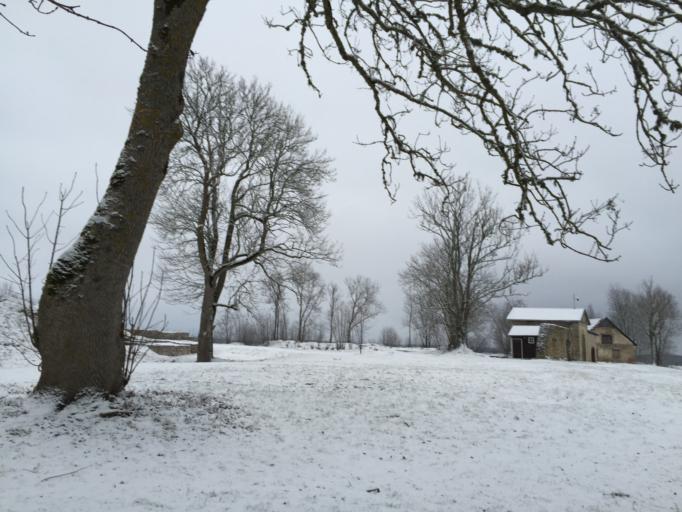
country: EE
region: Laeaene
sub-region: Lihula vald
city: Lihula
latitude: 58.6938
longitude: 23.8389
